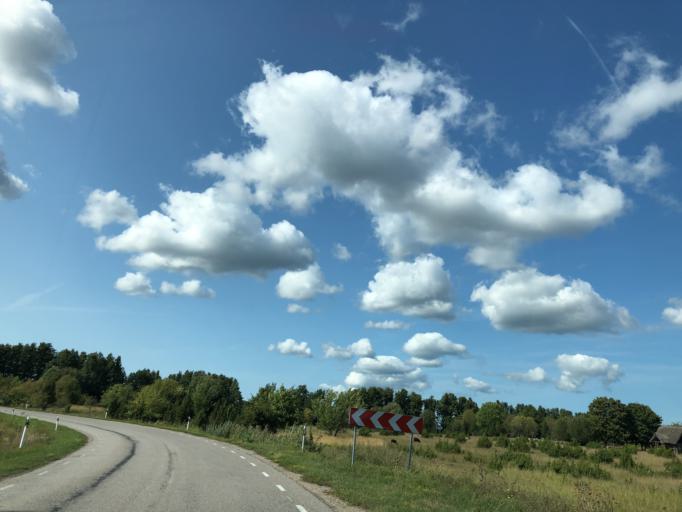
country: EE
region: Hiiumaa
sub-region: Kaerdla linn
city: Kardla
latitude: 58.7996
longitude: 22.7637
